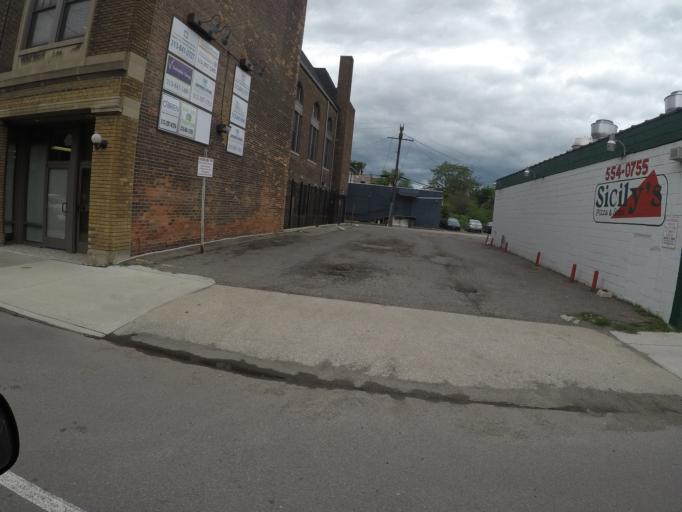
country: US
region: Michigan
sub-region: Wayne County
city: Detroit
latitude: 42.3235
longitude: -83.0877
